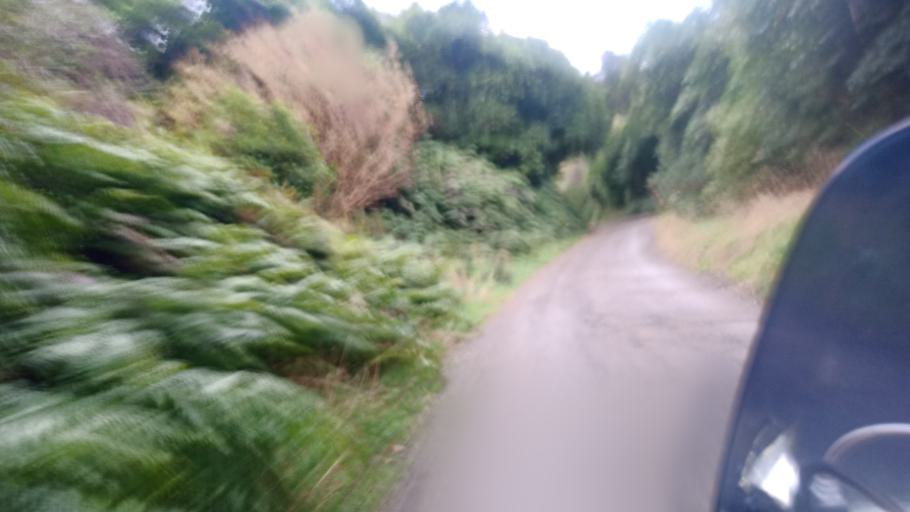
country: NZ
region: Hawke's Bay
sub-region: Wairoa District
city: Wairoa
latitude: -38.7323
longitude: 177.0910
